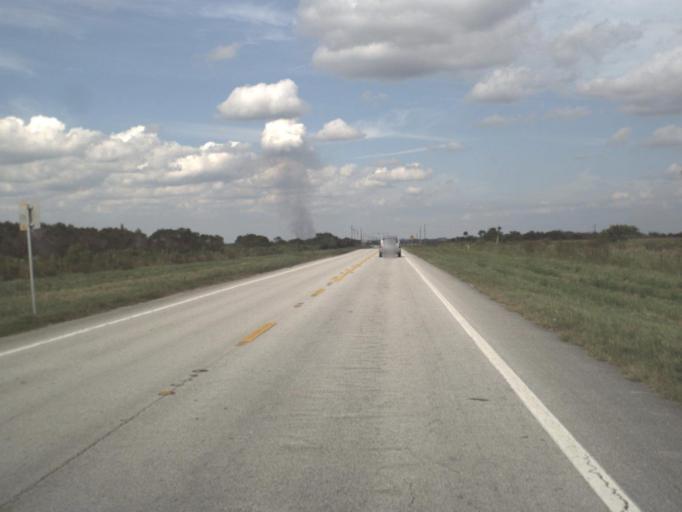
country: US
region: Florida
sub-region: Okeechobee County
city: Cypress Quarters
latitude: 27.4440
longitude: -80.8108
